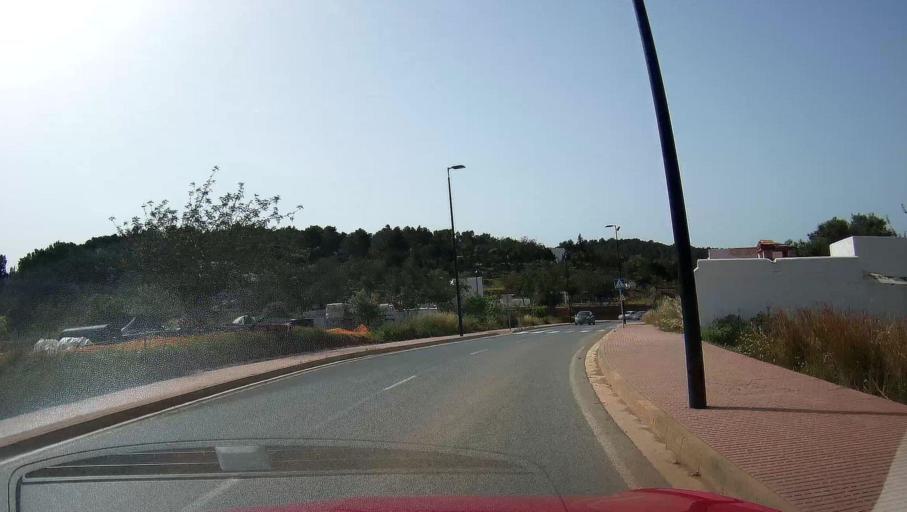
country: ES
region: Balearic Islands
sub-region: Illes Balears
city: Santa Eularia des Riu
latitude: 39.0345
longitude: 1.5660
